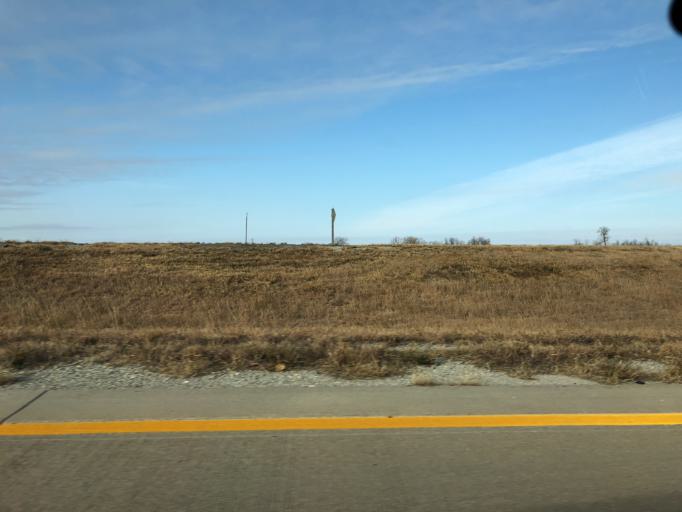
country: US
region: Kansas
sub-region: Reno County
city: South Hutchinson
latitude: 38.0554
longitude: -97.9855
